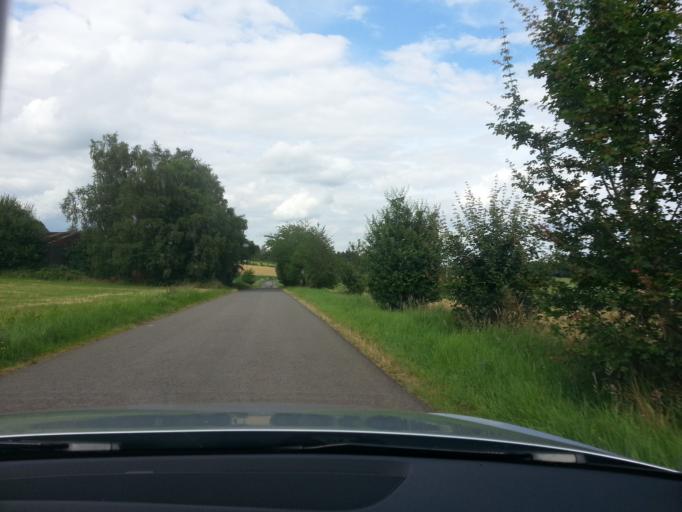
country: DE
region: Saarland
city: Marpingen
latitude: 49.4519
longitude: 7.0842
